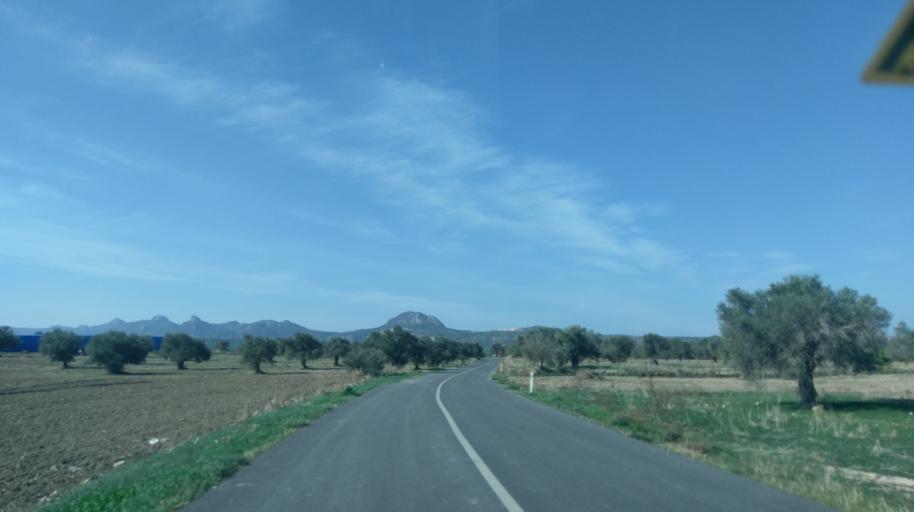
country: CY
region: Ammochostos
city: Leonarisso
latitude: 35.4065
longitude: 34.0101
